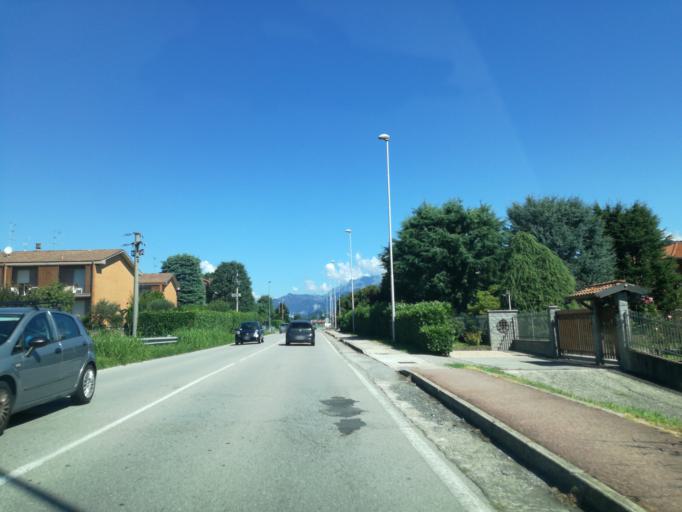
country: IT
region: Lombardy
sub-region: Provincia di Lecco
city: Imbersago
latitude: 45.7041
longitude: 9.4494
